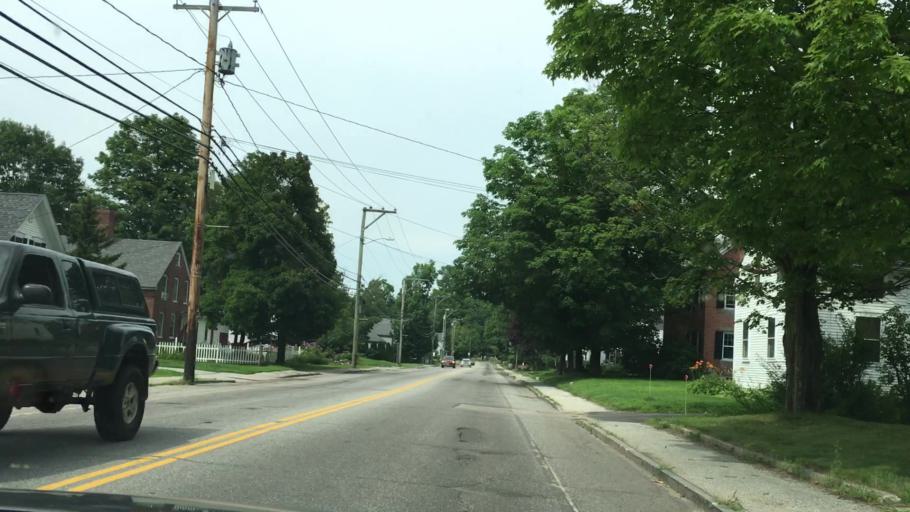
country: US
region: New Hampshire
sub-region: Hillsborough County
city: Peterborough
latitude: 42.8793
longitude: -71.9473
